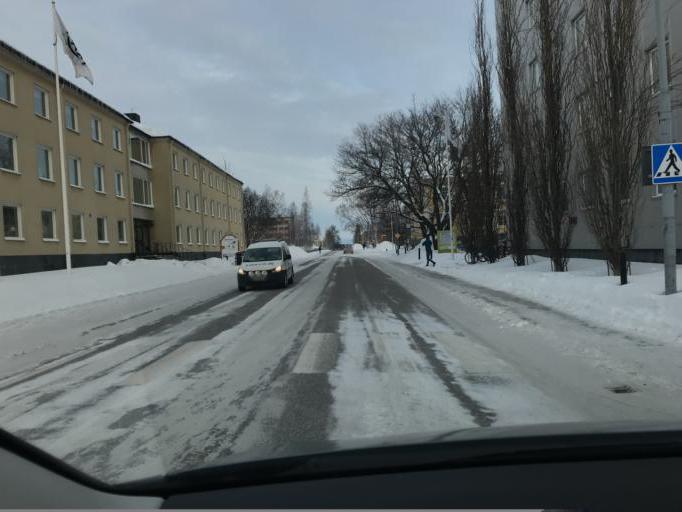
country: SE
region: Norrbotten
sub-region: Lulea Kommun
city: Lulea
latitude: 65.5810
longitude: 22.1375
